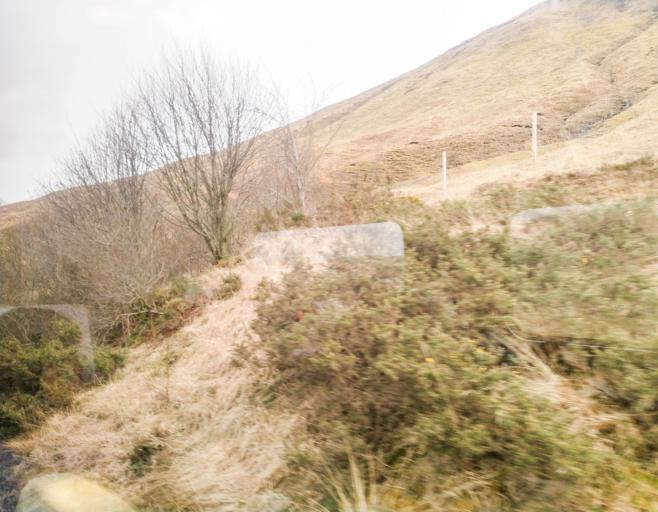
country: GB
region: Scotland
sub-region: Argyll and Bute
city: Garelochhead
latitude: 56.4719
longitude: -4.7175
